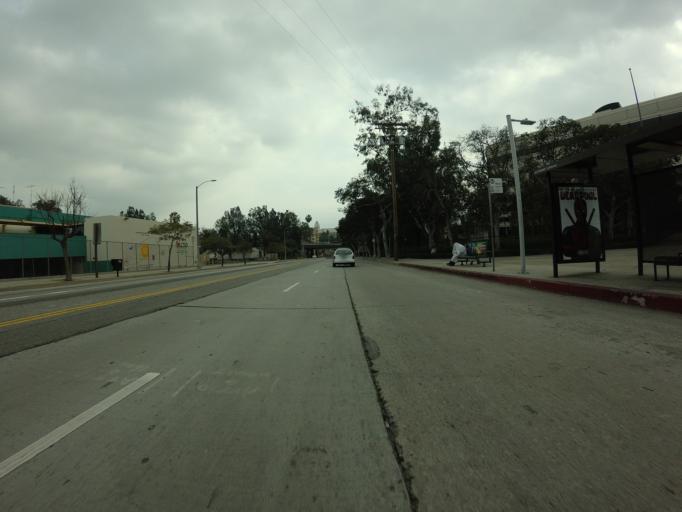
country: US
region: California
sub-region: Los Angeles County
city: Los Angeles
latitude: 34.0629
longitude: -118.2512
